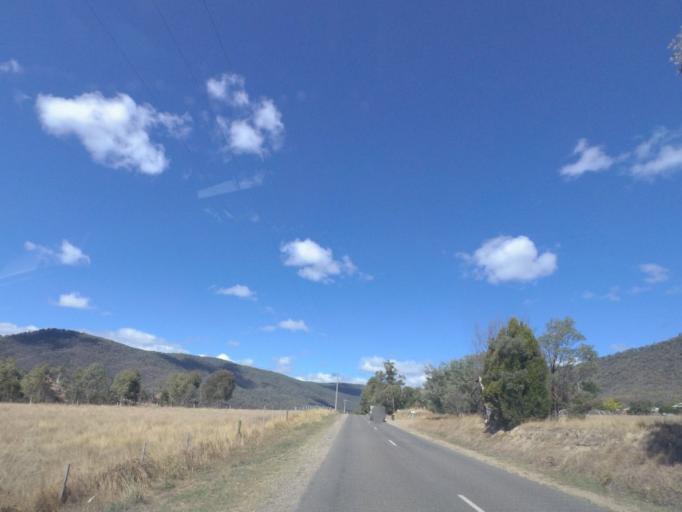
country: AU
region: Victoria
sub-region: Murrindindi
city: Alexandra
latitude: -37.2970
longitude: 145.8265
